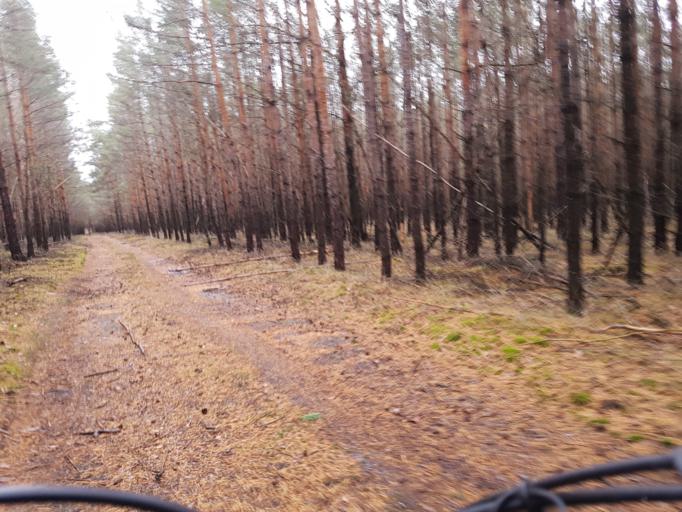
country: DE
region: Brandenburg
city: Schilda
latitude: 51.6214
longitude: 13.3830
